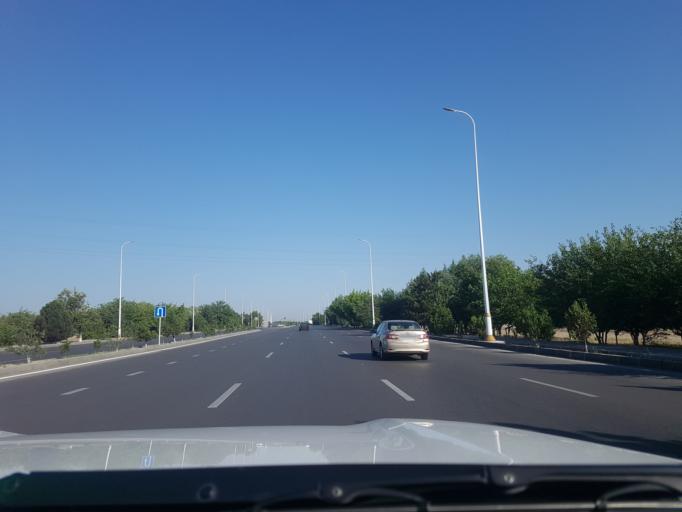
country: TM
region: Ahal
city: Abadan
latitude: 38.0052
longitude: 58.2901
